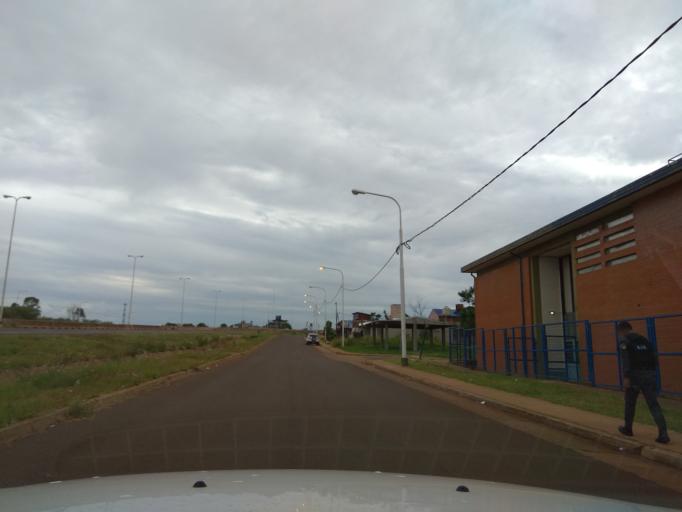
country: AR
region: Misiones
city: Garupa
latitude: -27.4500
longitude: -55.8552
